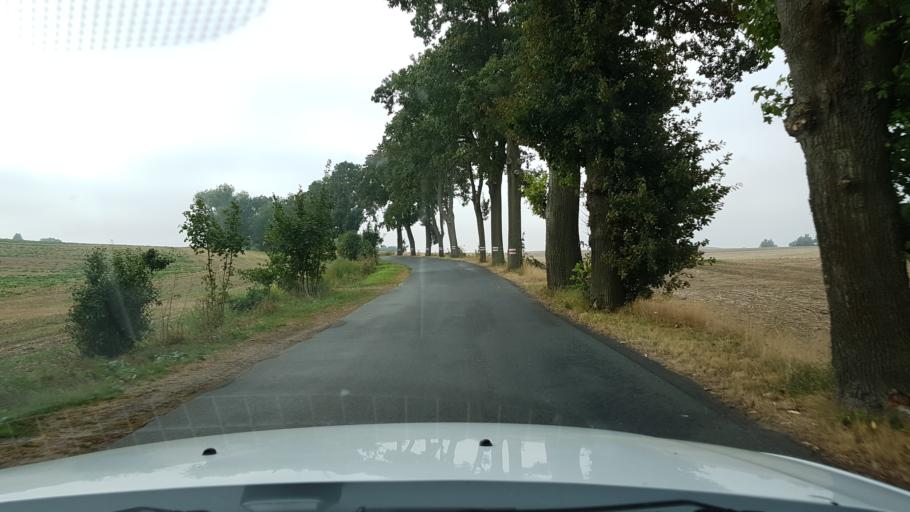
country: PL
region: West Pomeranian Voivodeship
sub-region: Powiat gryfinski
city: Moryn
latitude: 52.8870
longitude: 14.3778
